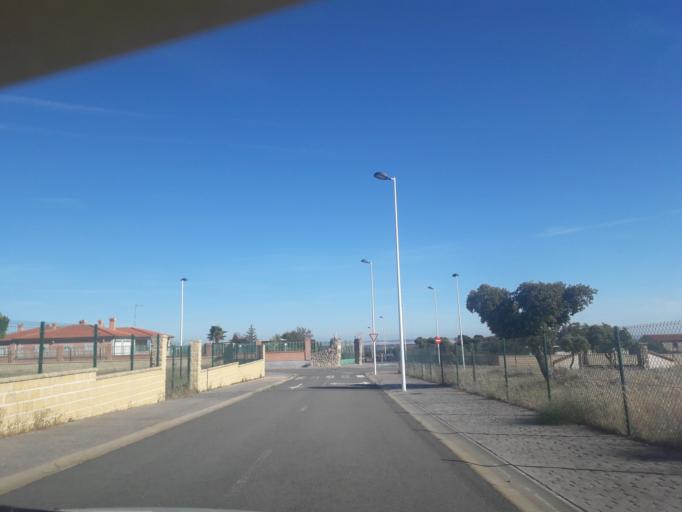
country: ES
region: Castille and Leon
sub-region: Provincia de Salamanca
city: Martinamor
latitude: 40.8062
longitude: -5.6481
